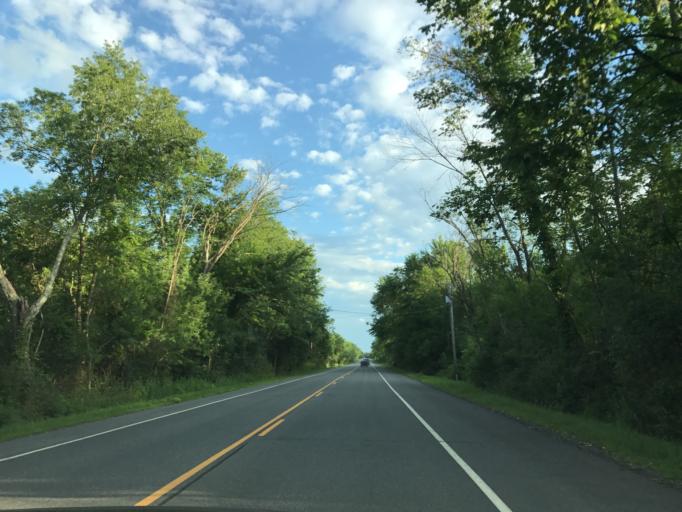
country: US
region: New York
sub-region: Saratoga County
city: Schuylerville
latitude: 43.0295
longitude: -73.5936
